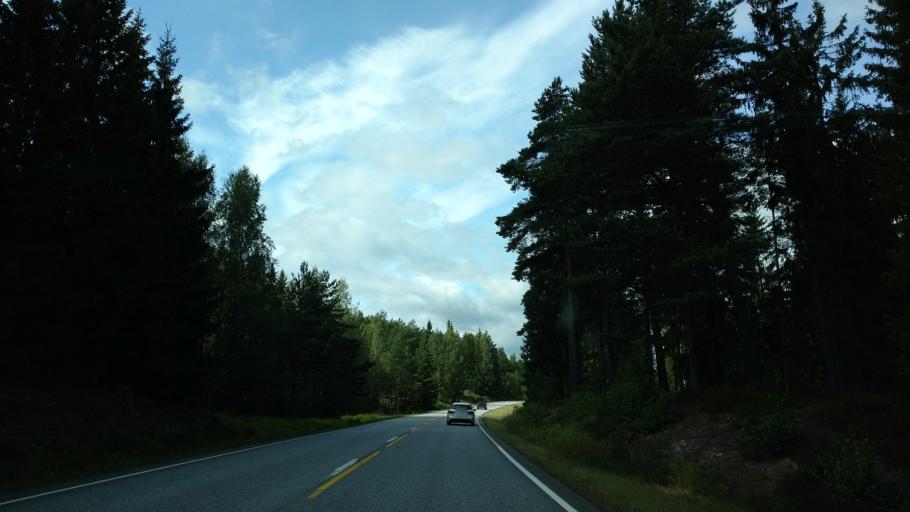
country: FI
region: Varsinais-Suomi
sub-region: Salo
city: Saerkisalo
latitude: 60.1770
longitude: 22.9243
